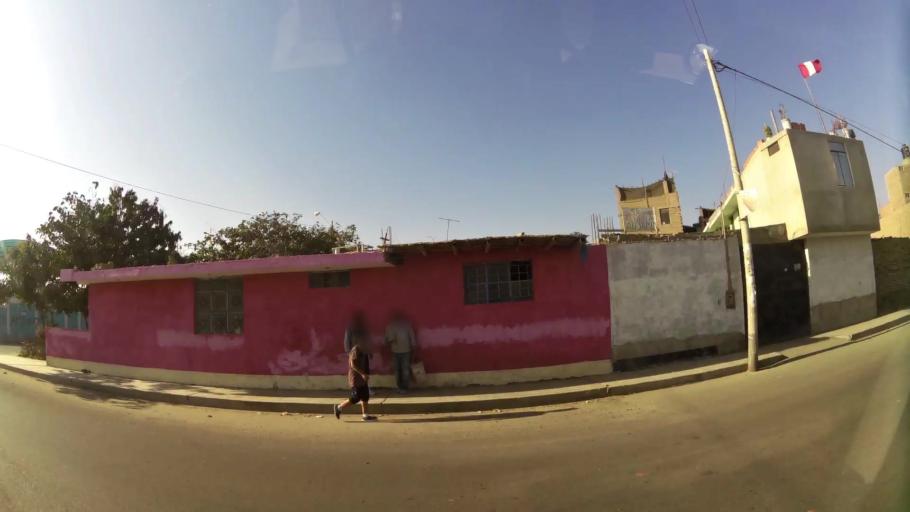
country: PE
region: Ica
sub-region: Provincia de Ica
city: La Tinguina
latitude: -14.0510
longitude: -75.6985
